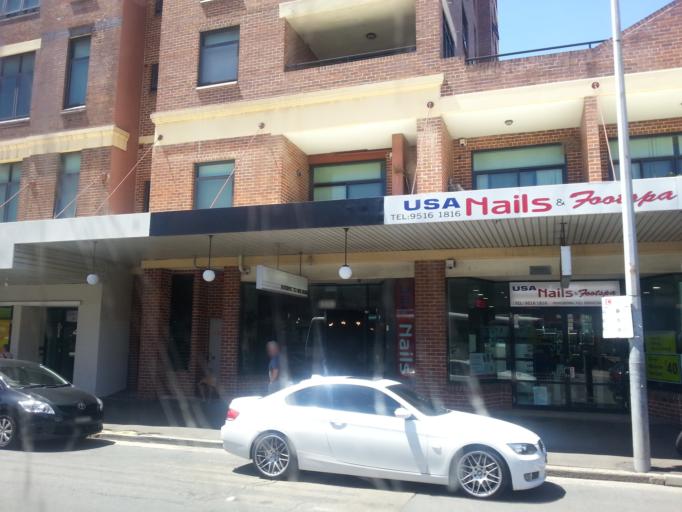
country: AU
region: New South Wales
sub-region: City of Sydney
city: Darlington
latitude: -33.8927
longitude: 151.1859
